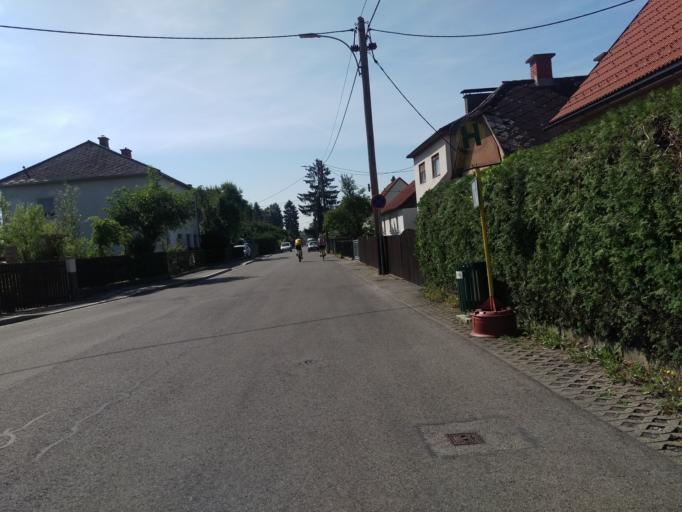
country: AT
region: Styria
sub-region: Politischer Bezirk Graz-Umgebung
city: Feldkirchen bei Graz
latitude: 47.0276
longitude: 15.4554
